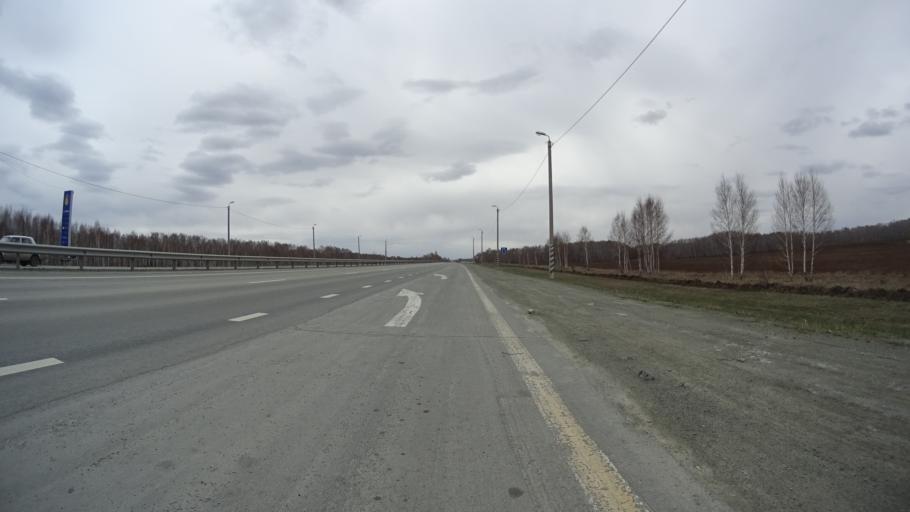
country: RU
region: Chelyabinsk
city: Yemanzhelinka
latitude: 54.8327
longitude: 61.3120
